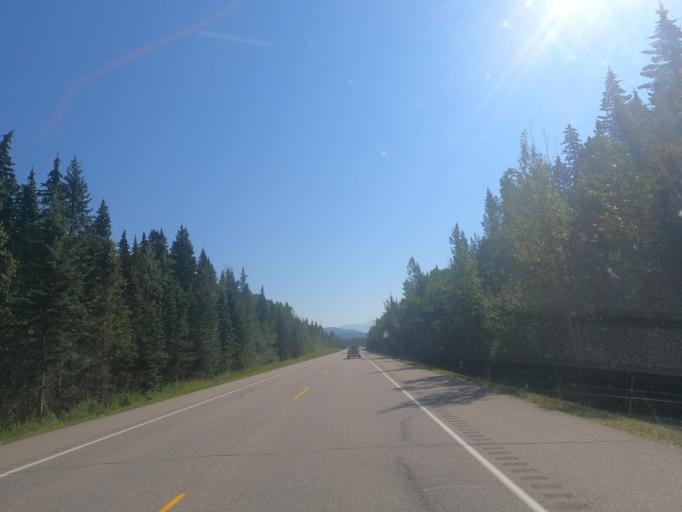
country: CA
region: Alberta
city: Jasper Park Lodge
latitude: 52.8766
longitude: -118.3244
